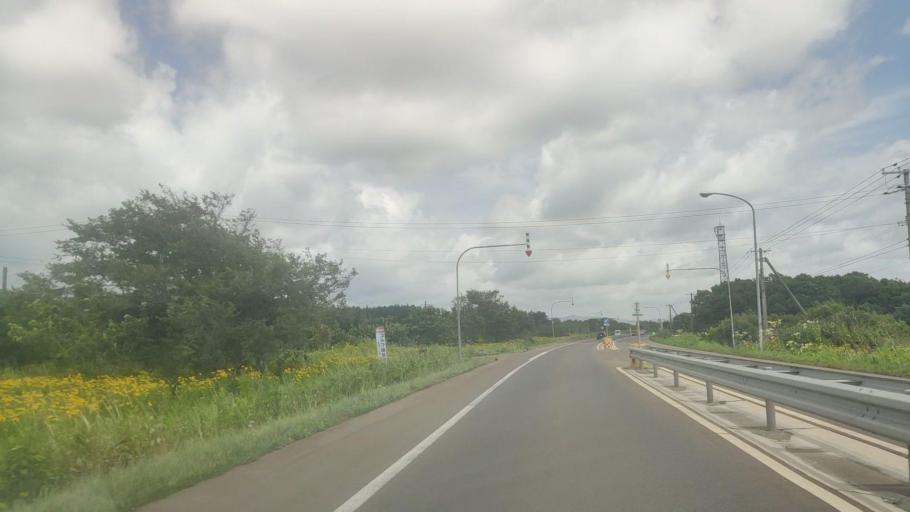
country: JP
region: Hokkaido
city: Niseko Town
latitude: 42.4542
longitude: 140.3324
